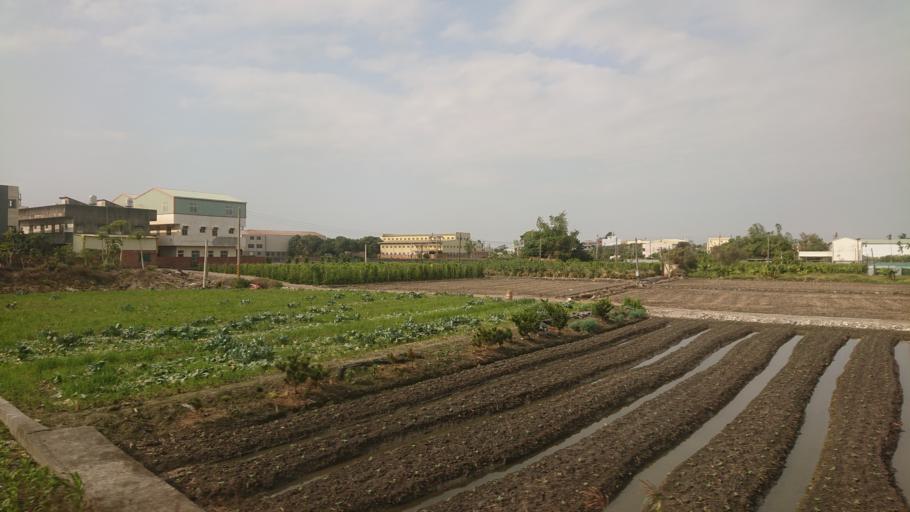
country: TW
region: Taiwan
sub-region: Nantou
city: Nantou
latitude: 23.9303
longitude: 120.5709
